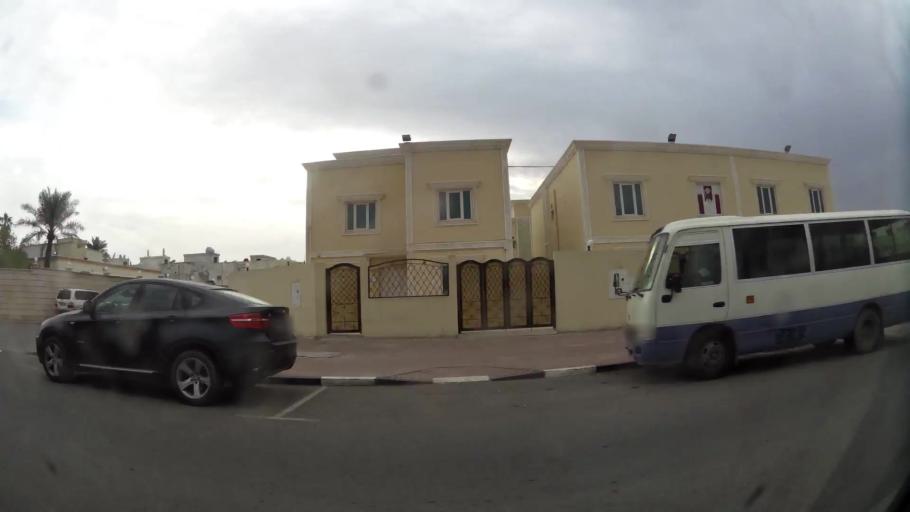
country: QA
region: Baladiyat ad Dawhah
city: Doha
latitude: 25.2721
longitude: 51.4950
